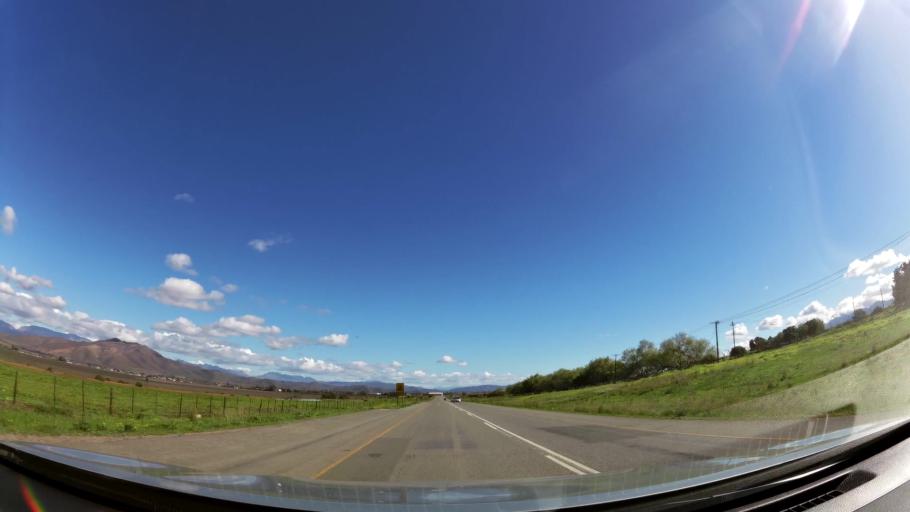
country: ZA
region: Western Cape
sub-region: Cape Winelands District Municipality
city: Ashton
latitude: -33.8382
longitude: 20.0290
